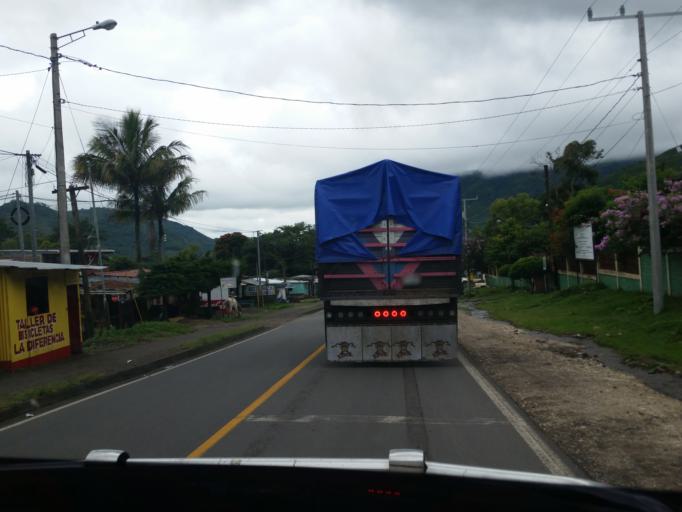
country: NI
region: Jinotega
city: Jinotega
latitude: 13.0846
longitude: -85.9934
